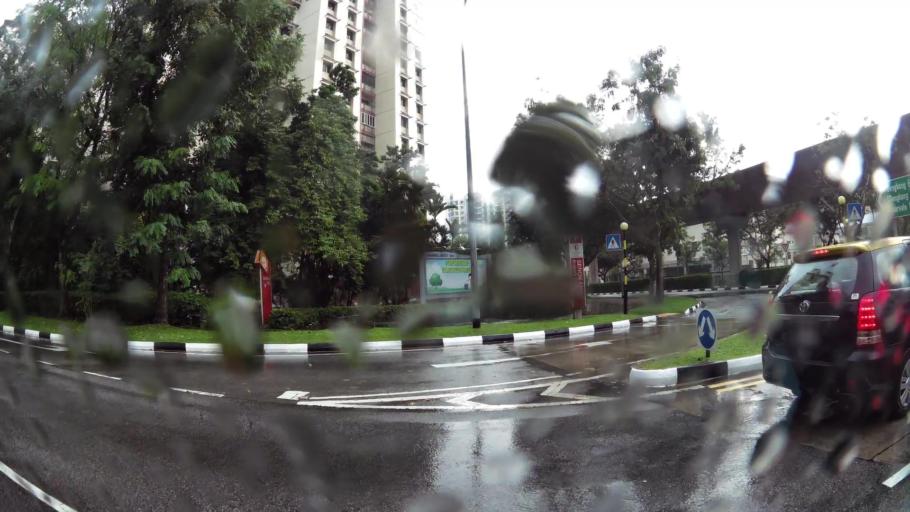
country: MY
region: Johor
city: Kampung Pasir Gudang Baru
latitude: 1.3831
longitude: 103.8988
